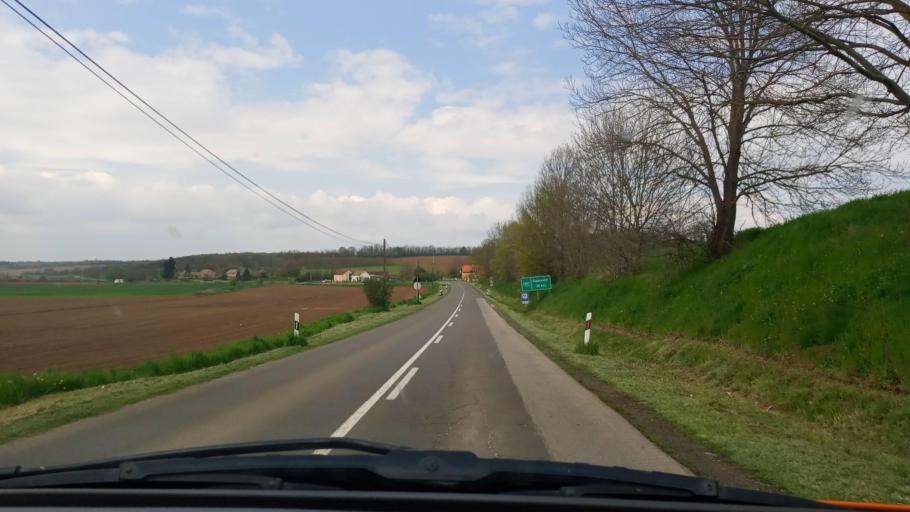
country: HU
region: Baranya
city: Sasd
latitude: 46.2619
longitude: 18.0911
